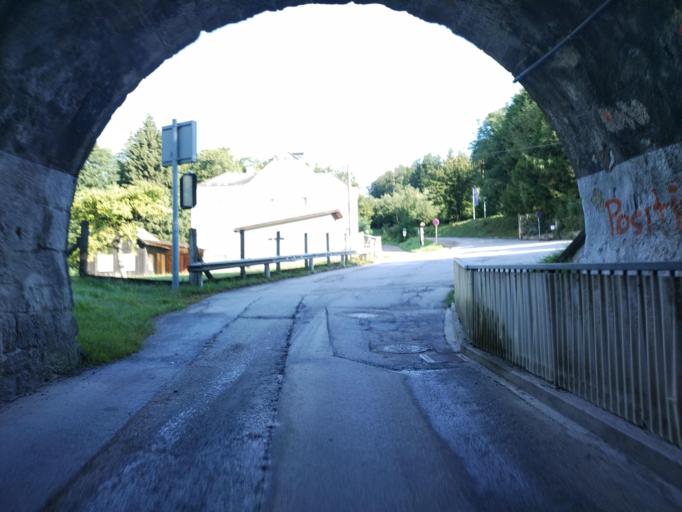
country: AT
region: Lower Austria
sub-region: Politischer Bezirk Wien-Umgebung
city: Pressbaum
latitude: 48.1825
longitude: 16.0799
